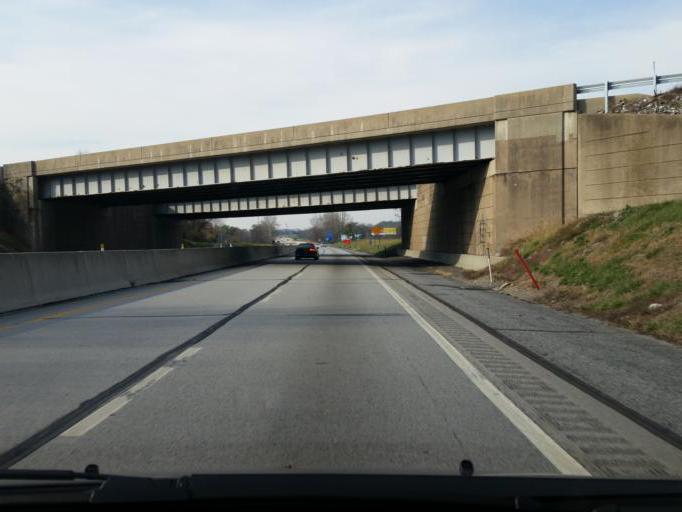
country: US
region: Pennsylvania
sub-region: Cumberland County
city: Schlusser
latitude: 40.2283
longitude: -77.1339
